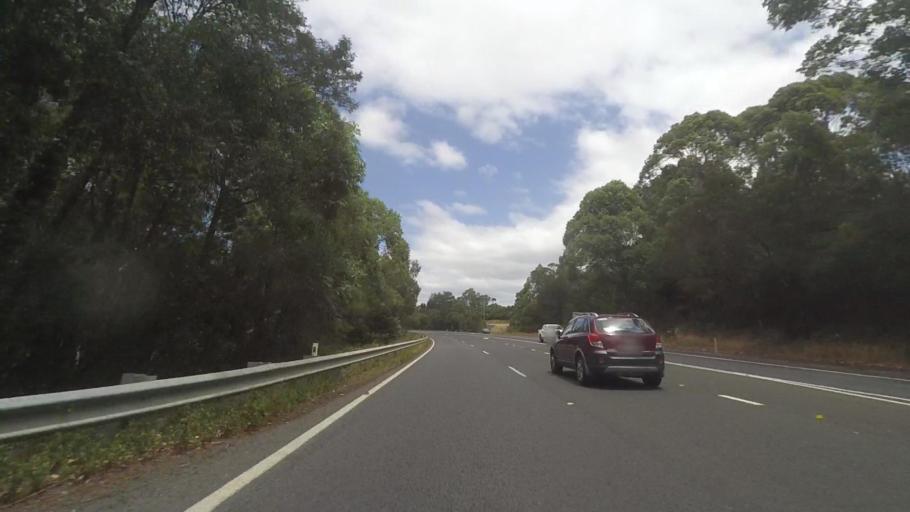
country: AU
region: New South Wales
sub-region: Shoalhaven Shire
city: Milton
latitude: -35.2469
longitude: 150.4244
